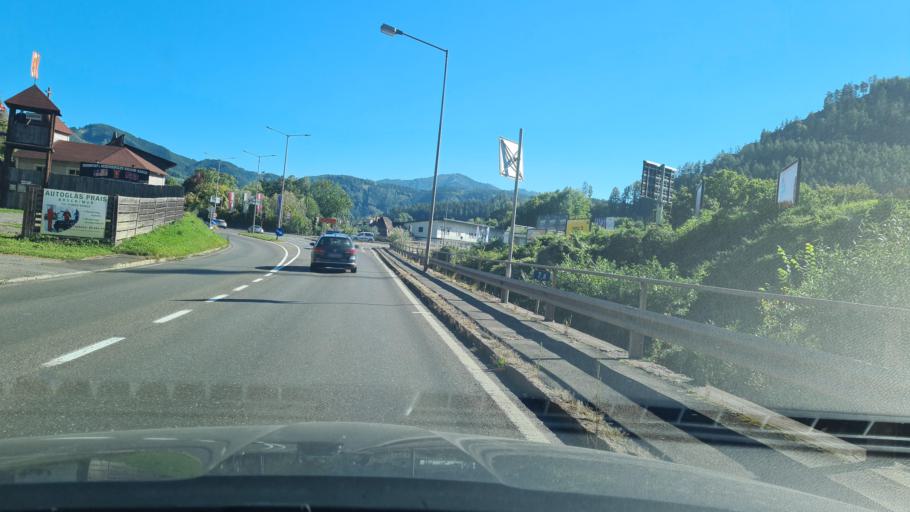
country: AT
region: Styria
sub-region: Politischer Bezirk Leoben
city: Leoben
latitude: 47.3774
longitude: 15.0799
